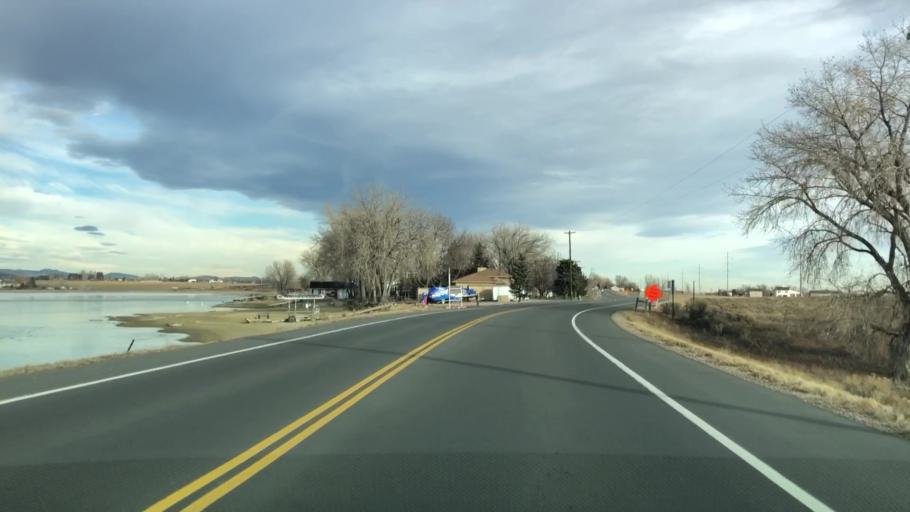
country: US
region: Colorado
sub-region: Larimer County
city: Loveland
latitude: 40.4412
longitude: -105.0457
